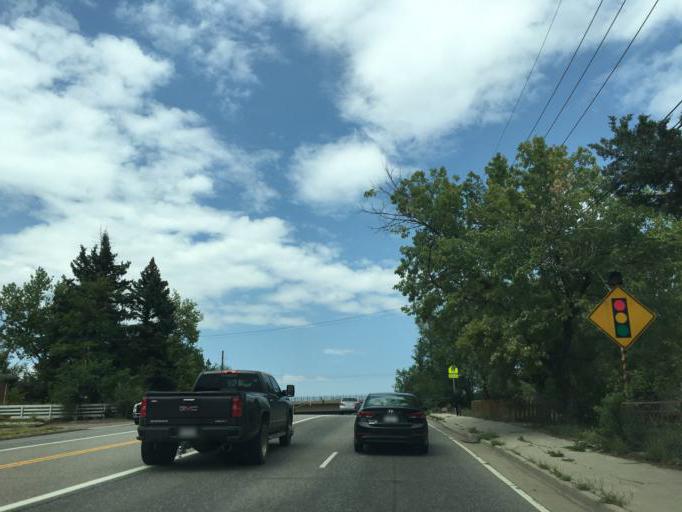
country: US
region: Colorado
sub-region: Jefferson County
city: Lakewood
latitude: 39.7350
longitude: -105.1095
